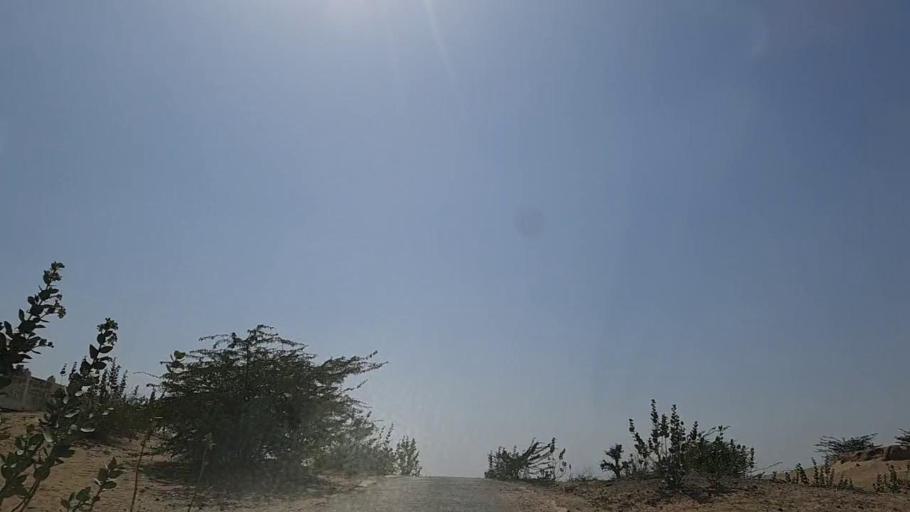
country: PK
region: Sindh
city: Mithi
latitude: 24.7066
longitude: 69.5908
